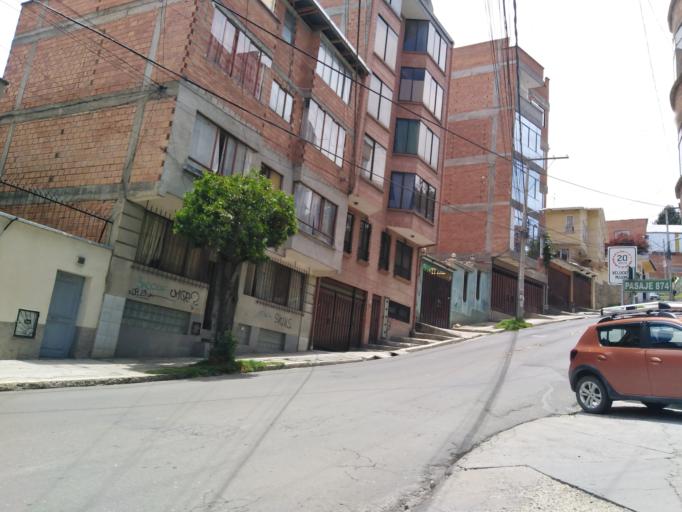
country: BO
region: La Paz
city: La Paz
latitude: -16.5086
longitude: -68.1372
